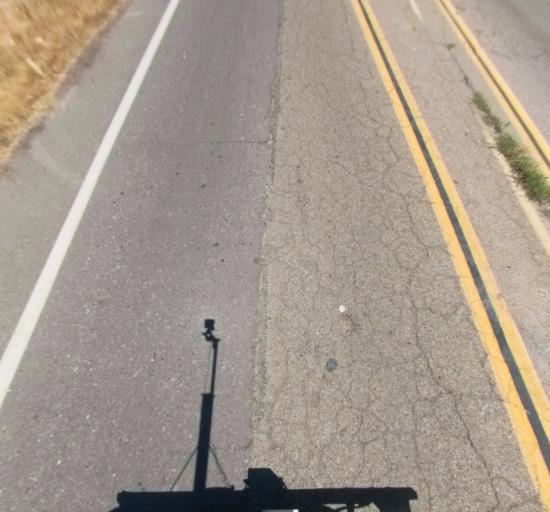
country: US
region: California
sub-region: Madera County
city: Madera Acres
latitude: 36.9965
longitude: -120.1082
